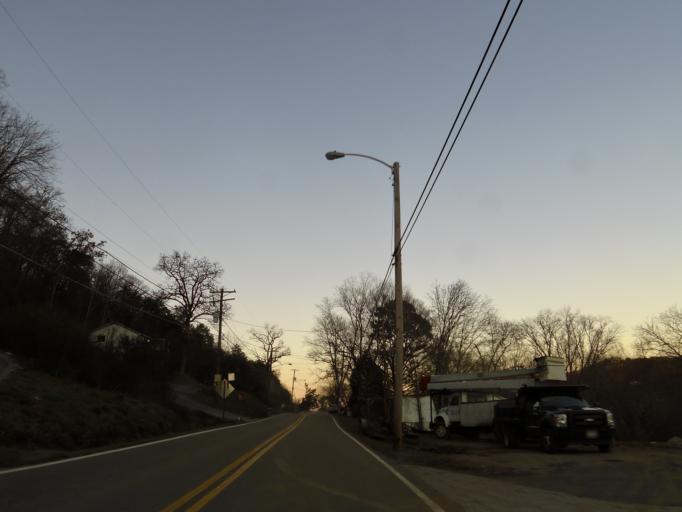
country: US
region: Tennessee
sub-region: Knox County
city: Knoxville
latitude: 36.0227
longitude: -83.9185
